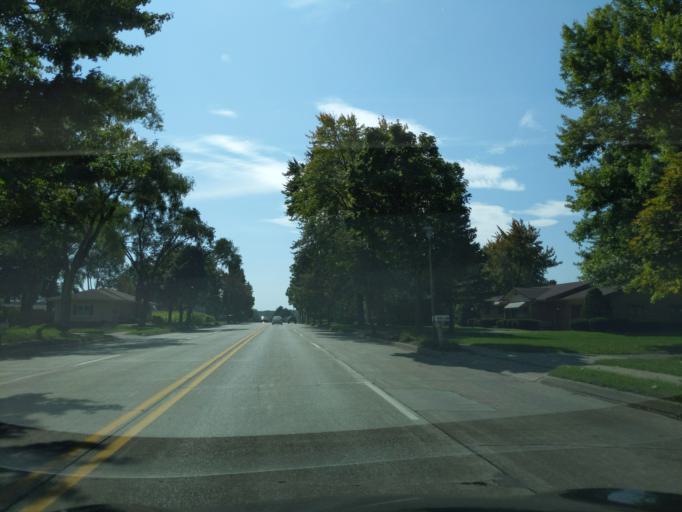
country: US
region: Michigan
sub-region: Saginaw County
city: Frankenmuth
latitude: 43.3195
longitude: -83.7405
